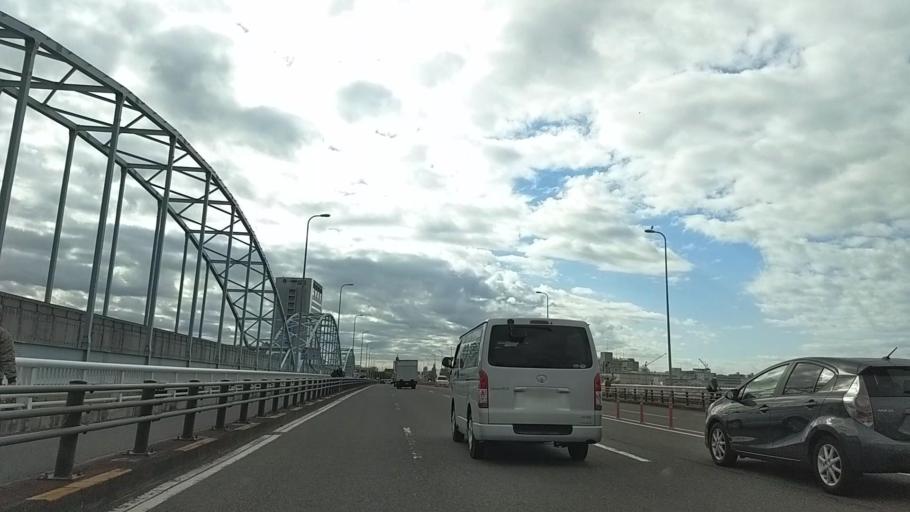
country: JP
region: Kanagawa
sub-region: Kawasaki-shi
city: Kawasaki
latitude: 35.5568
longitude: 139.6965
